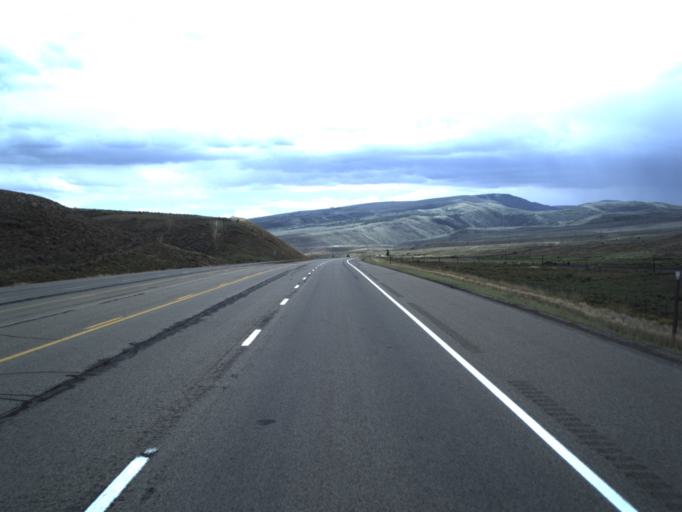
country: US
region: Utah
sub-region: Carbon County
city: Helper
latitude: 39.8719
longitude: -111.0335
